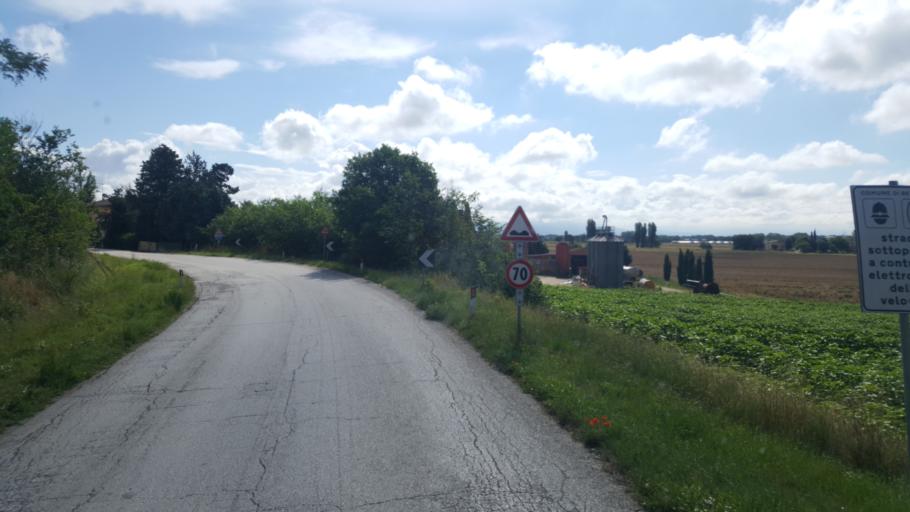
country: IT
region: Umbria
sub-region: Provincia di Perugia
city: Torgiano
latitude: 43.0377
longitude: 12.4651
